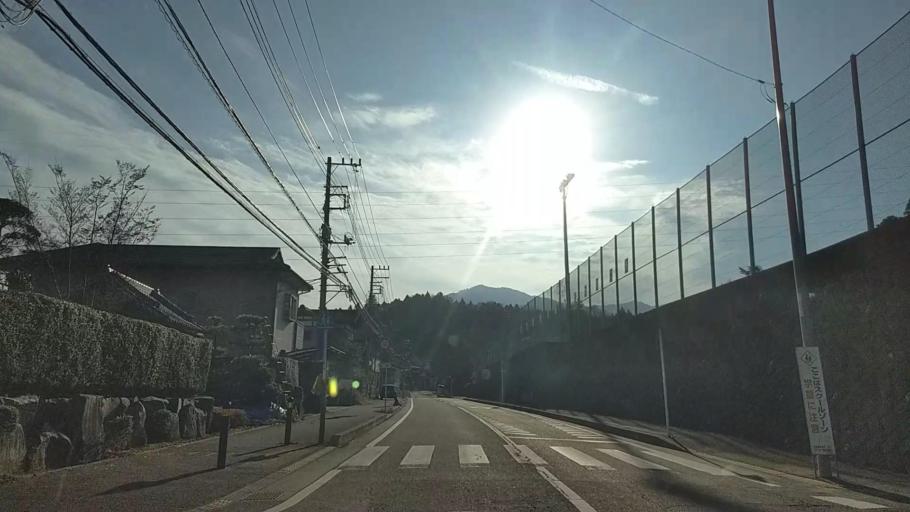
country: JP
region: Yamanashi
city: Uenohara
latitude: 35.5457
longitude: 139.2184
